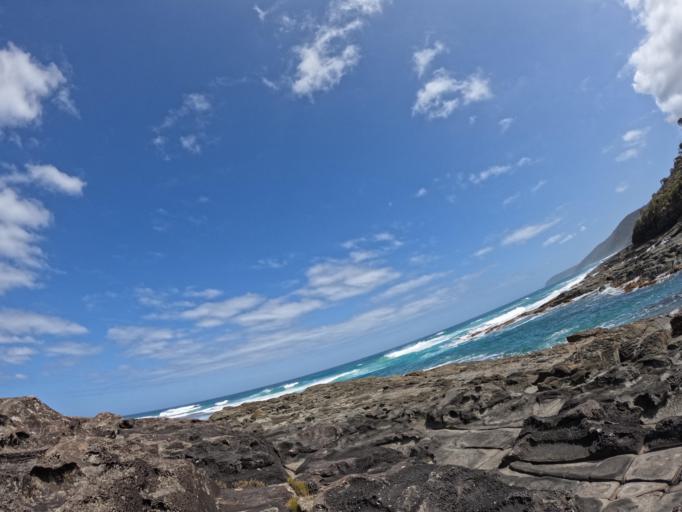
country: AU
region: Victoria
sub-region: Colac-Otway
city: Apollo Bay
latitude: -38.7927
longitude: 143.6229
